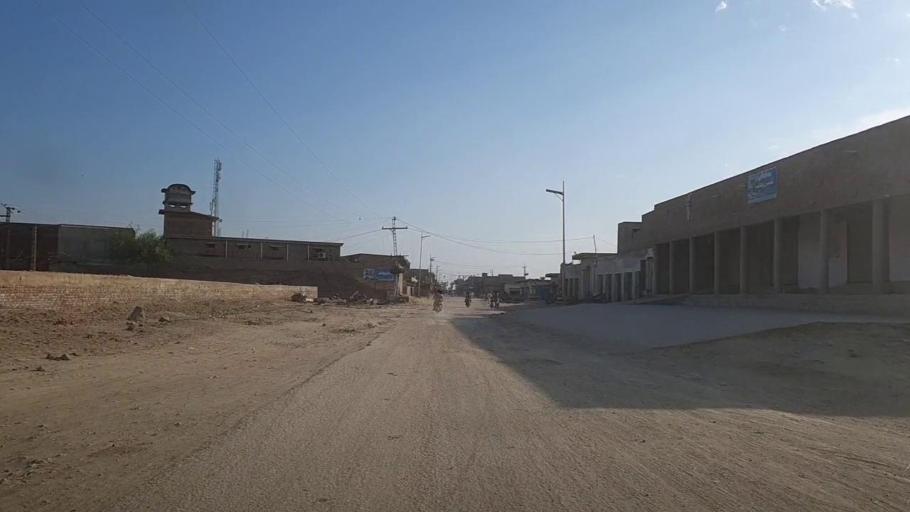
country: PK
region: Sindh
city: Thul
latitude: 28.1834
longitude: 68.7265
